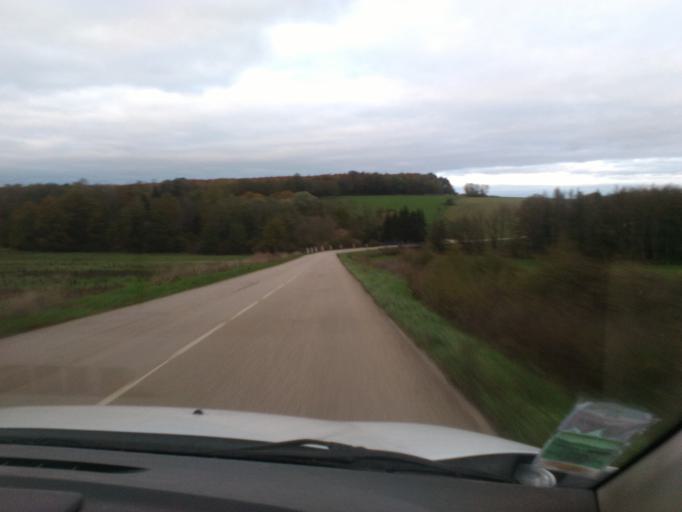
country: FR
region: Lorraine
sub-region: Departement des Vosges
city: Darnieulles
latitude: 48.2478
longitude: 6.3459
